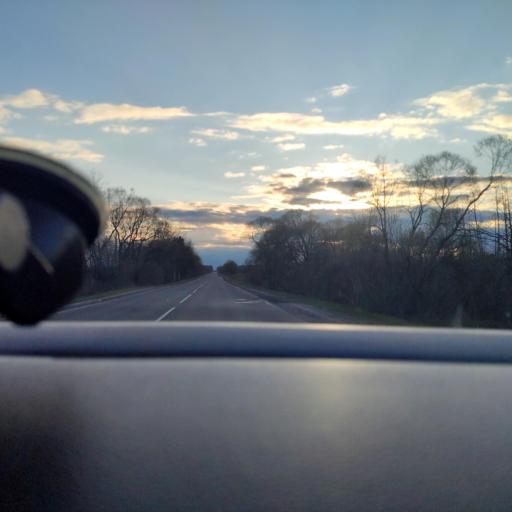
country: RU
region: Moskovskaya
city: Krasnyy Tkach
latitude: 55.4282
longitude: 39.2322
